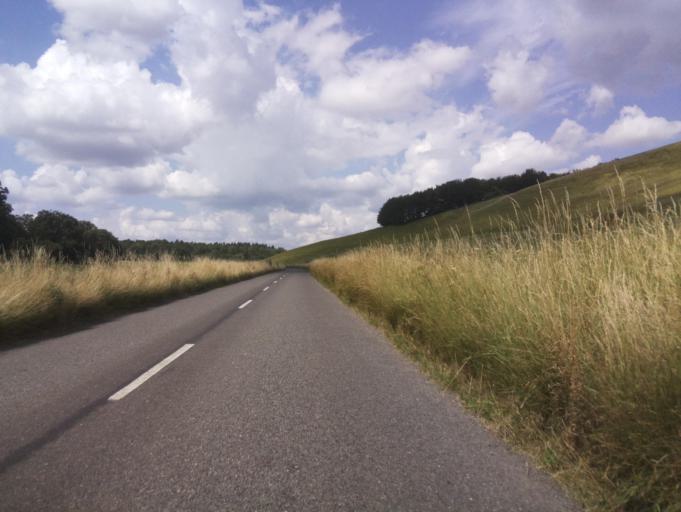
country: GB
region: England
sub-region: Borough of Swindon
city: Bishopstone
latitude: 51.5404
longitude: -1.5918
